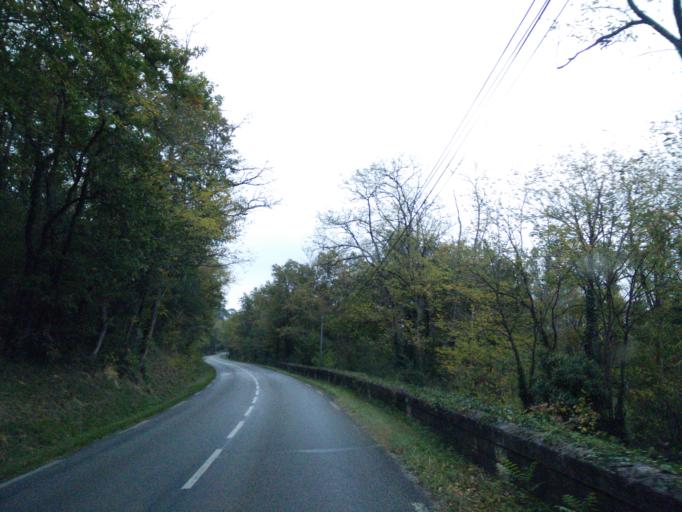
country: FR
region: Midi-Pyrenees
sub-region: Departement du Lot
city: Gourdon
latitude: 44.7829
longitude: 1.3180
